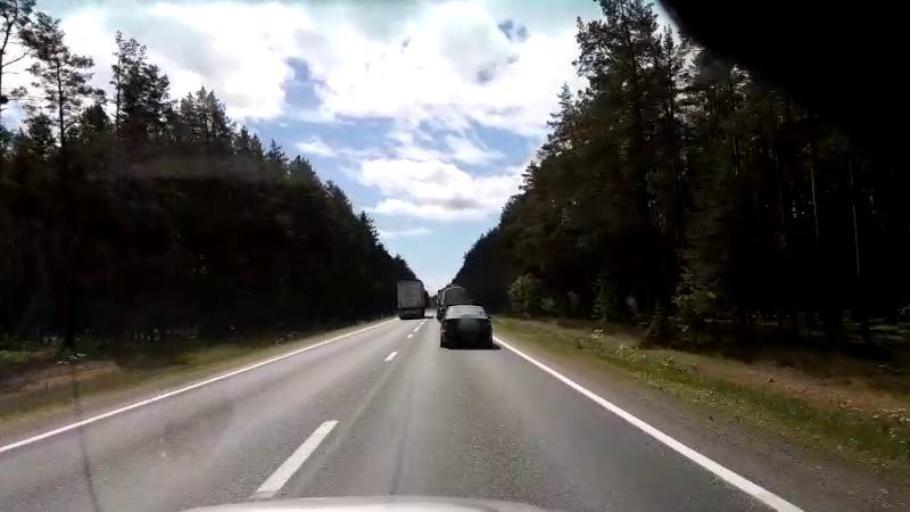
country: LV
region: Salacgrivas
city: Salacgriva
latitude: 57.5380
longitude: 24.4316
